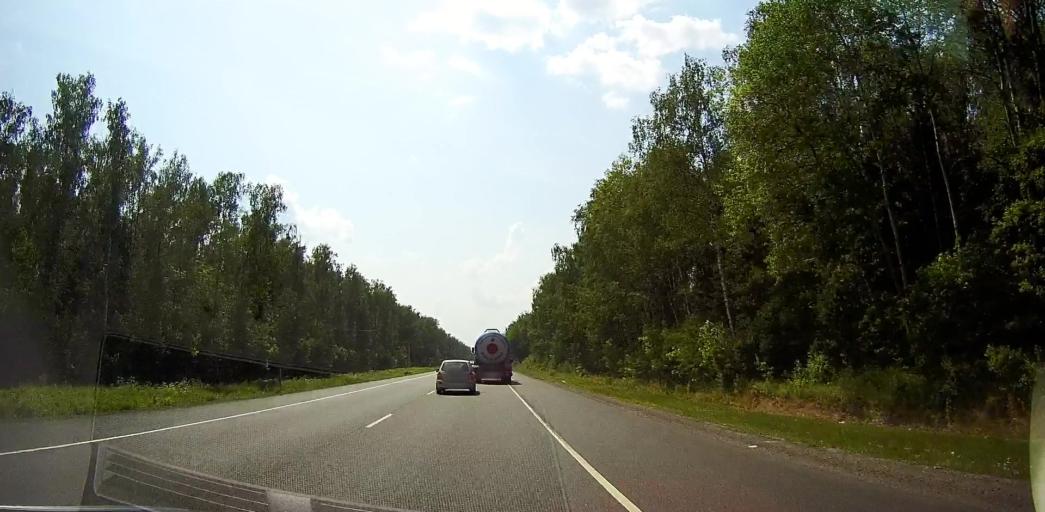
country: RU
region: Moskovskaya
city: Meshcherino
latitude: 55.2160
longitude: 38.3928
